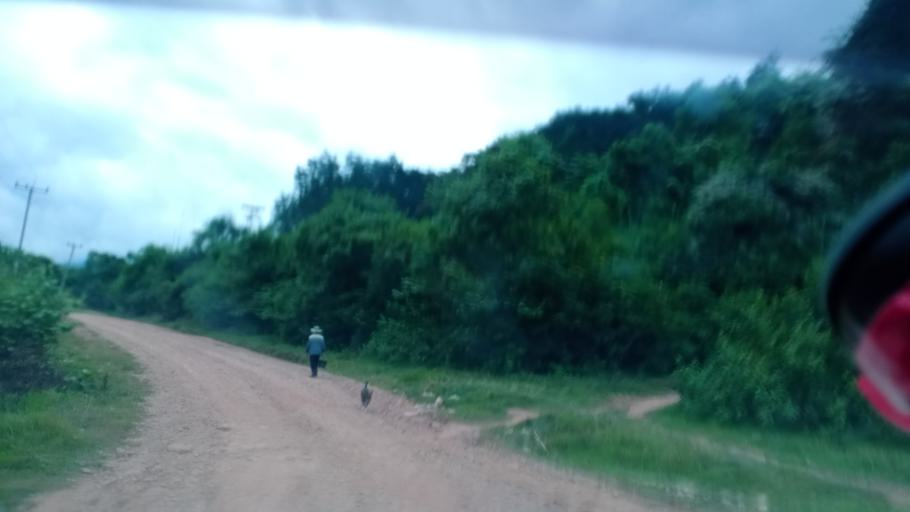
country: TH
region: Changwat Bueng Kan
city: Pak Khat
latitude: 18.7152
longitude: 103.2123
